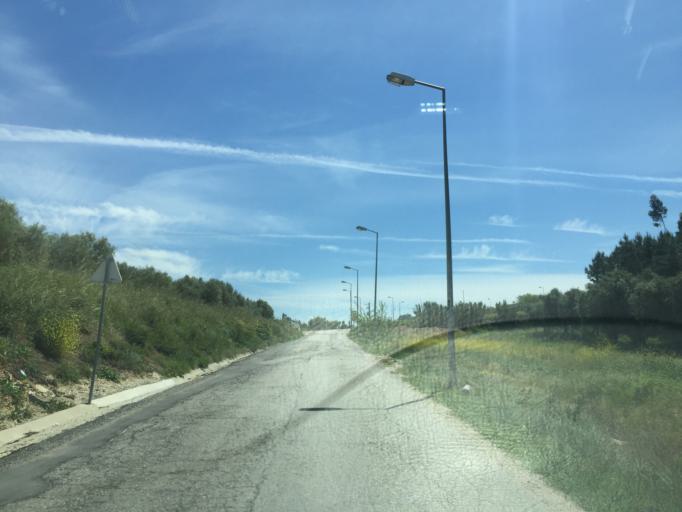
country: PT
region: Leiria
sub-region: Pombal
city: Lourical
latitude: 40.0679
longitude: -8.7299
